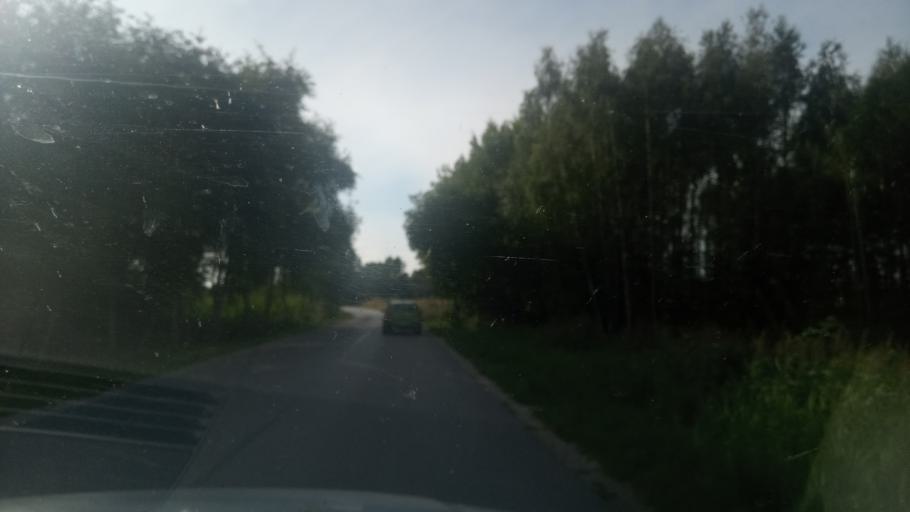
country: PL
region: Greater Poland Voivodeship
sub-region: Powiat pilski
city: Lobzenica
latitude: 53.2489
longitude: 17.2814
